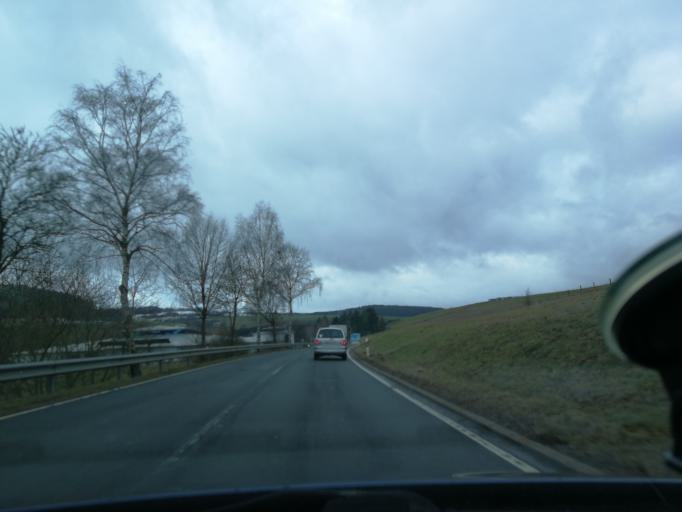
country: DE
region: Rheinland-Pfalz
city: Dreis-Bruck
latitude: 50.2678
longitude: 6.7823
